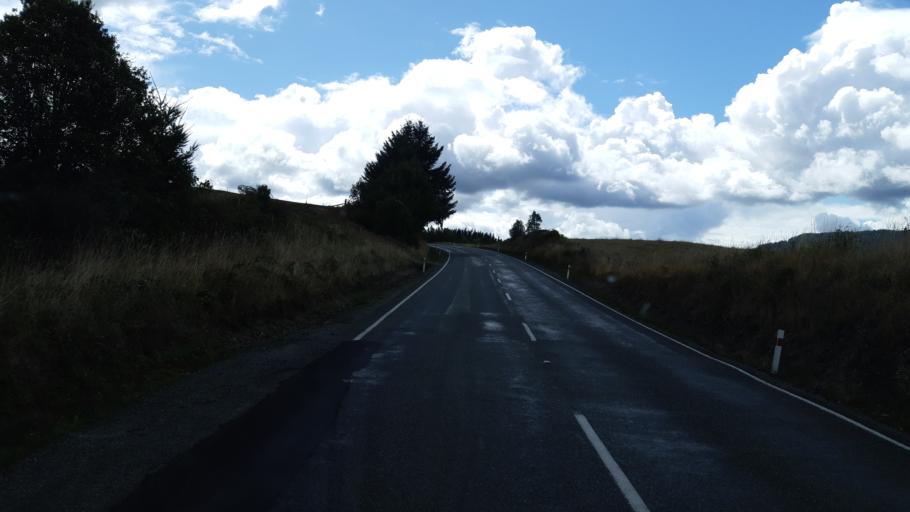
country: NZ
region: Tasman
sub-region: Tasman District
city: Wakefield
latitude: -41.5589
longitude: 172.7839
